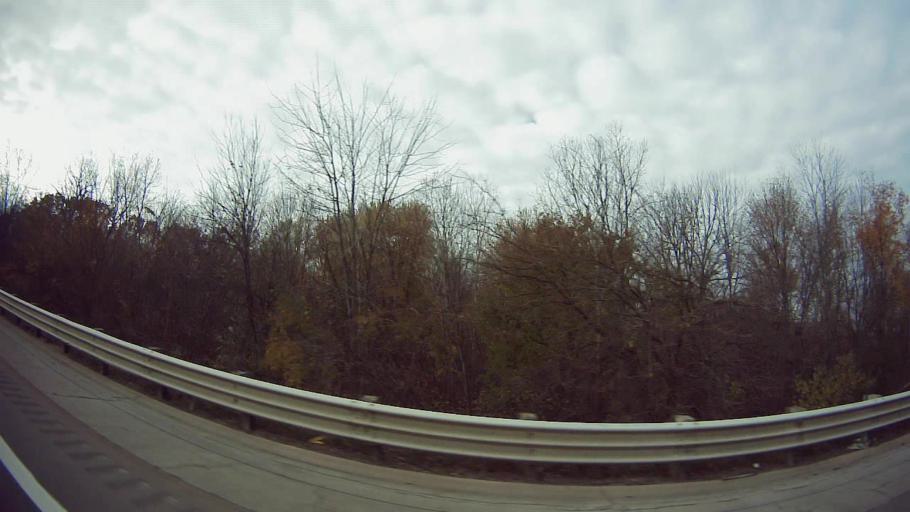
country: US
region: Michigan
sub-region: Monroe County
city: Carleton
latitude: 42.0727
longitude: -83.3675
